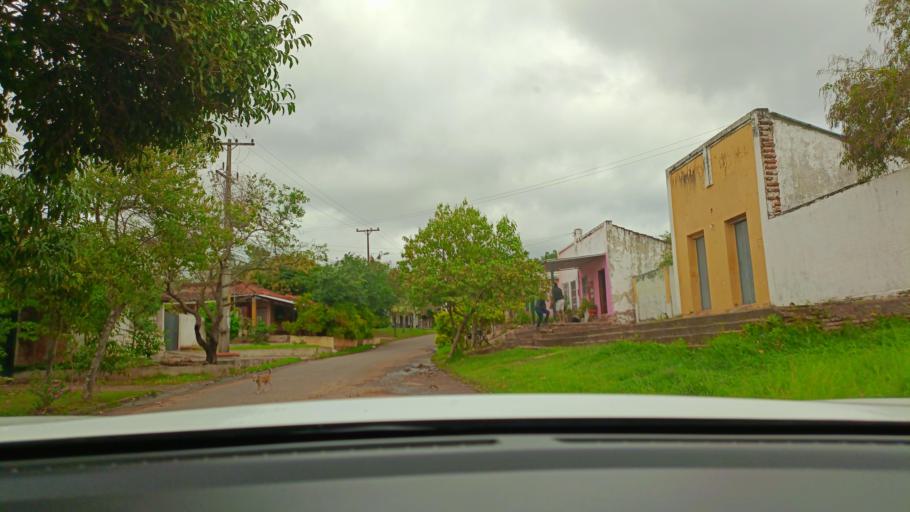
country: PY
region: San Pedro
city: Guayaybi
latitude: -24.6686
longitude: -56.4496
